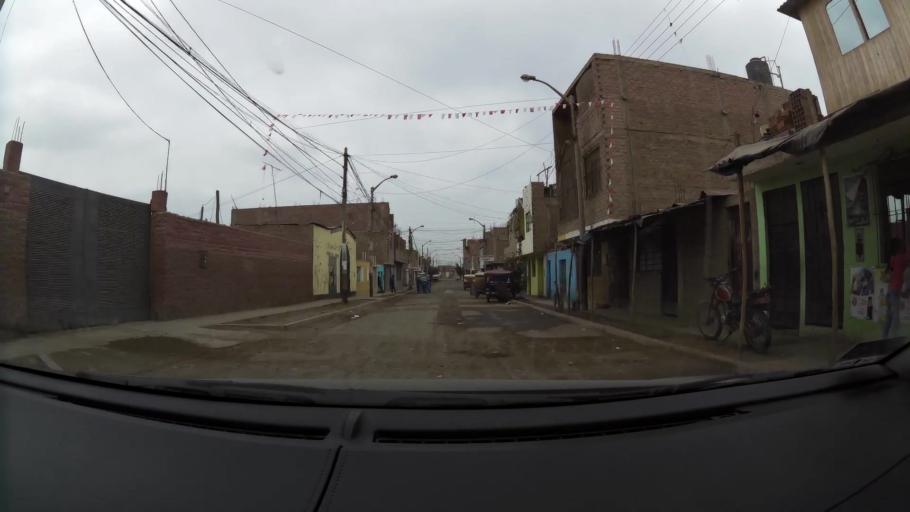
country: PE
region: Lima
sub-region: Provincia de Huaral
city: Huaral
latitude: -11.4979
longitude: -77.2014
